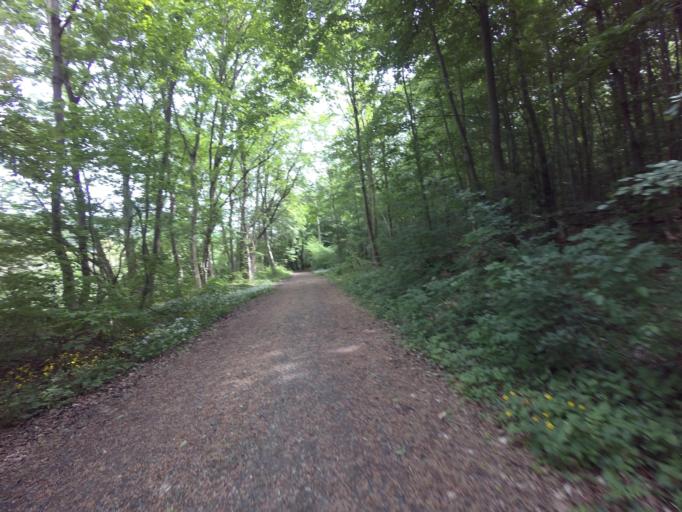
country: DE
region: Lower Saxony
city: Erkerode
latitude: 52.2061
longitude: 10.7424
